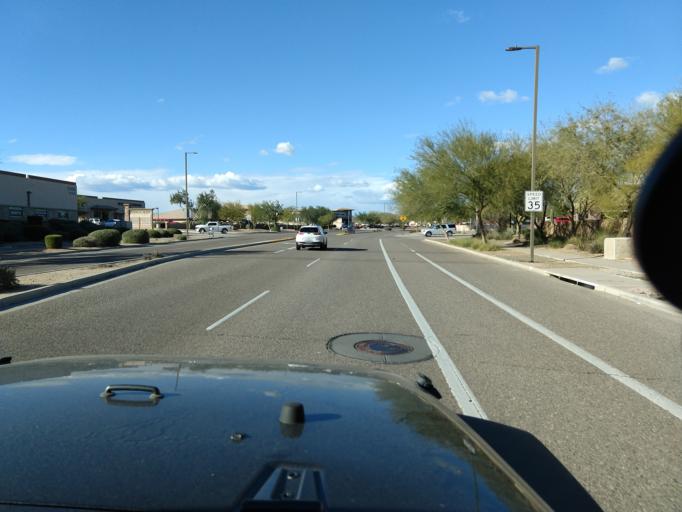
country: US
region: Arizona
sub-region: Maricopa County
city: Anthem
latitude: 33.7960
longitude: -112.1176
